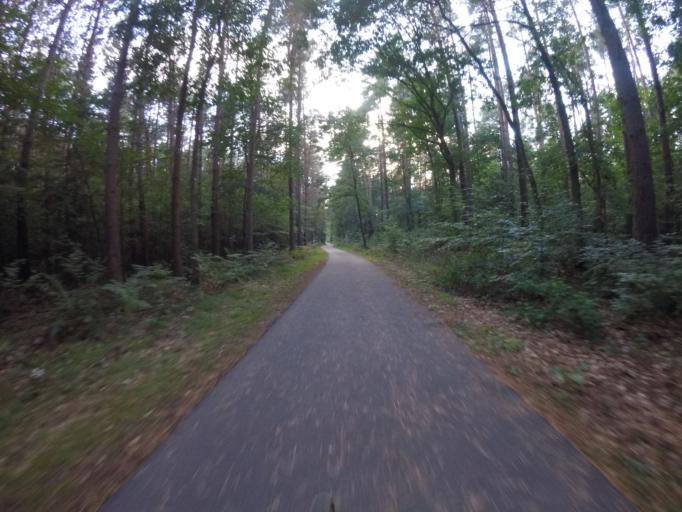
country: DE
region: Brandenburg
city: Petershagen
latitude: 52.5541
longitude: 13.8127
